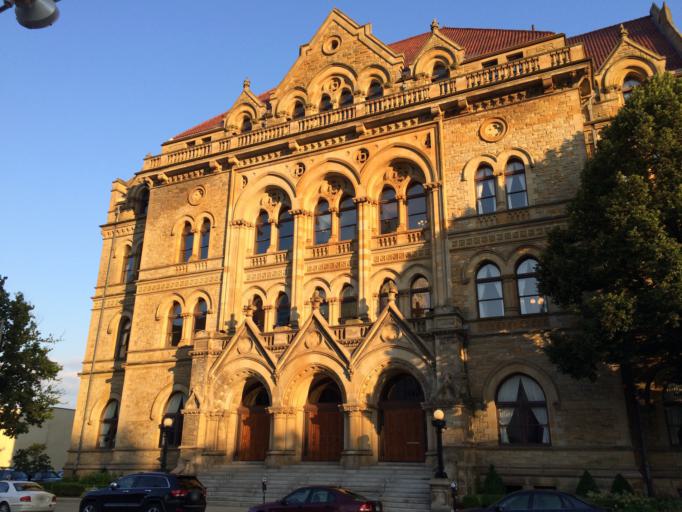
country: US
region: Ohio
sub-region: Franklin County
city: Columbus
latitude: 39.9607
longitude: -82.9973
